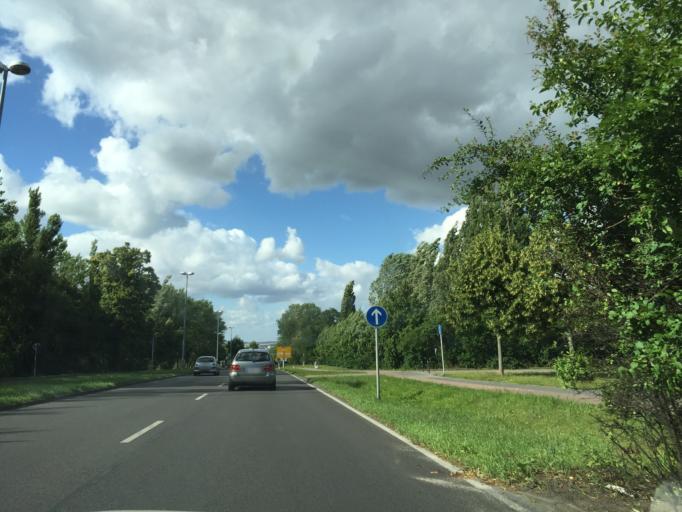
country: DE
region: Mecklenburg-Vorpommern
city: Neubrandenburg
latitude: 53.5269
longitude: 13.2620
